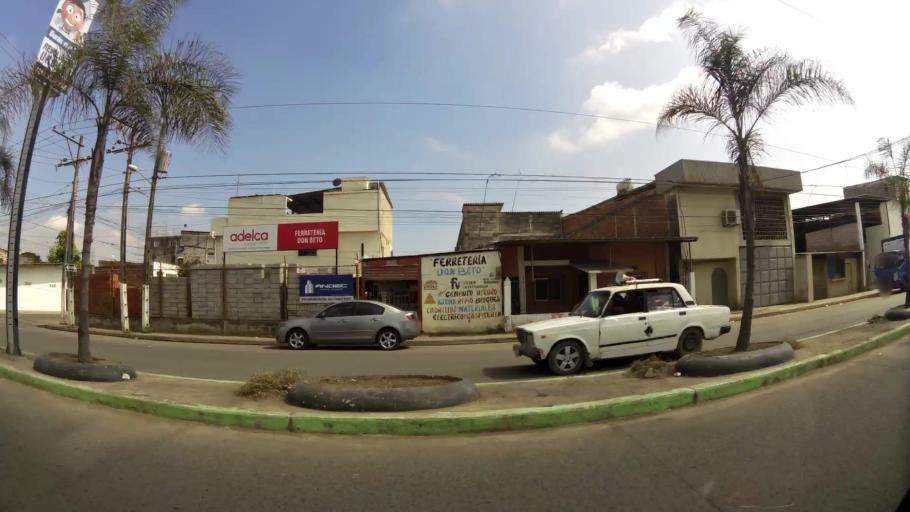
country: EC
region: Guayas
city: Eloy Alfaro
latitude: -2.1579
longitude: -79.8301
